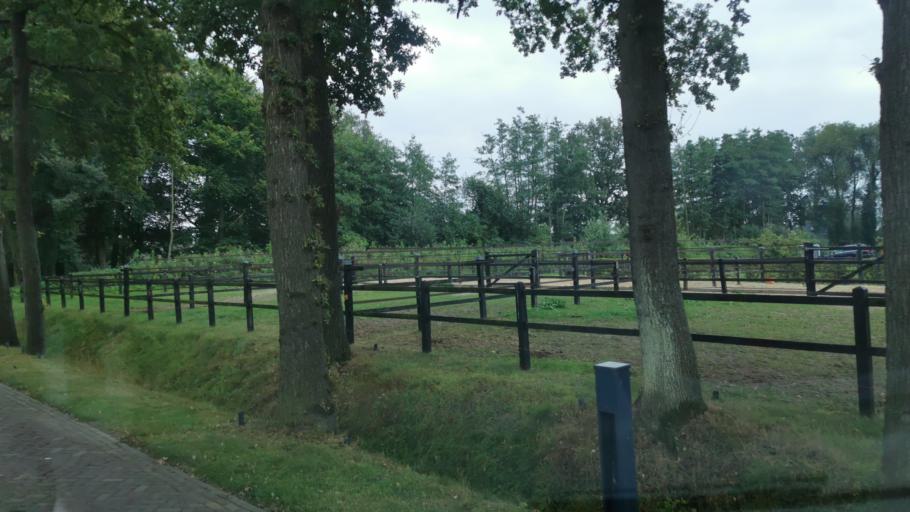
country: NL
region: Overijssel
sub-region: Gemeente Losser
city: Losser
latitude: 52.3264
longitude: 7.0058
